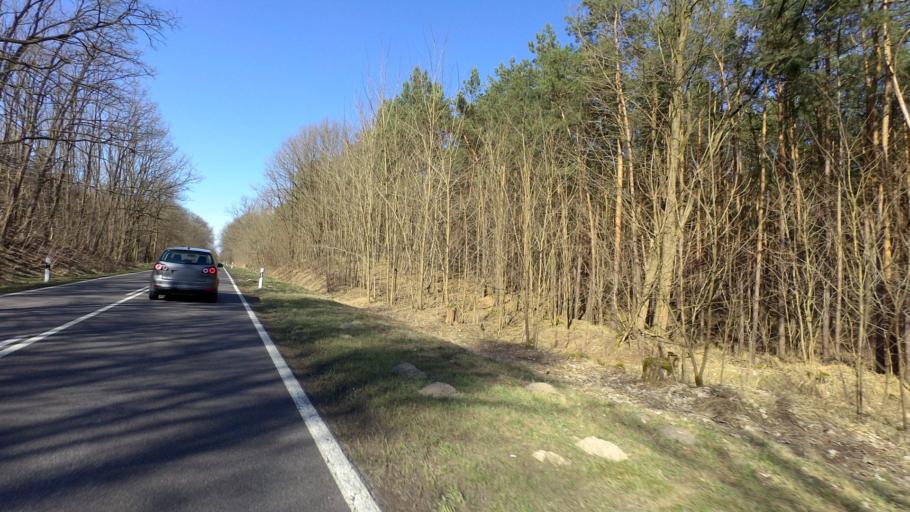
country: DE
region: Brandenburg
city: Eberswalde
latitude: 52.7985
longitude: 13.8366
